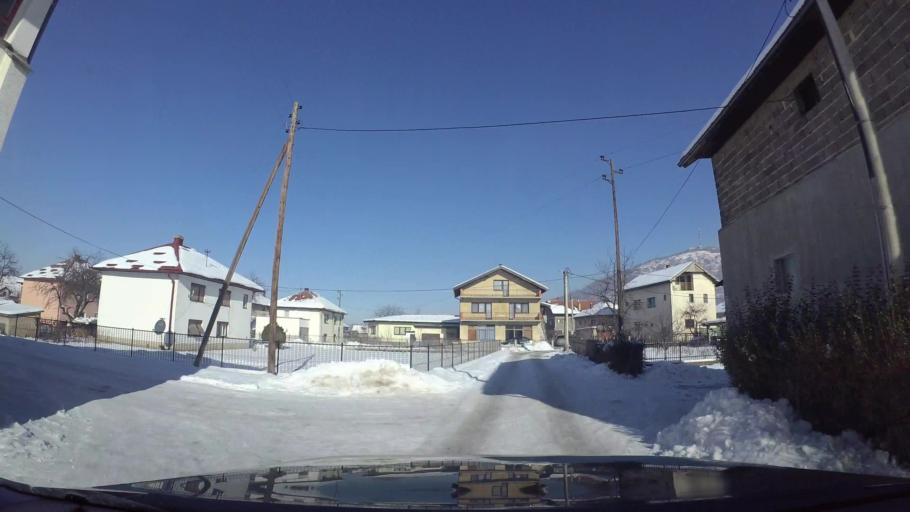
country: BA
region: Federation of Bosnia and Herzegovina
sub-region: Kanton Sarajevo
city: Sarajevo
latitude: 43.7988
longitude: 18.3474
